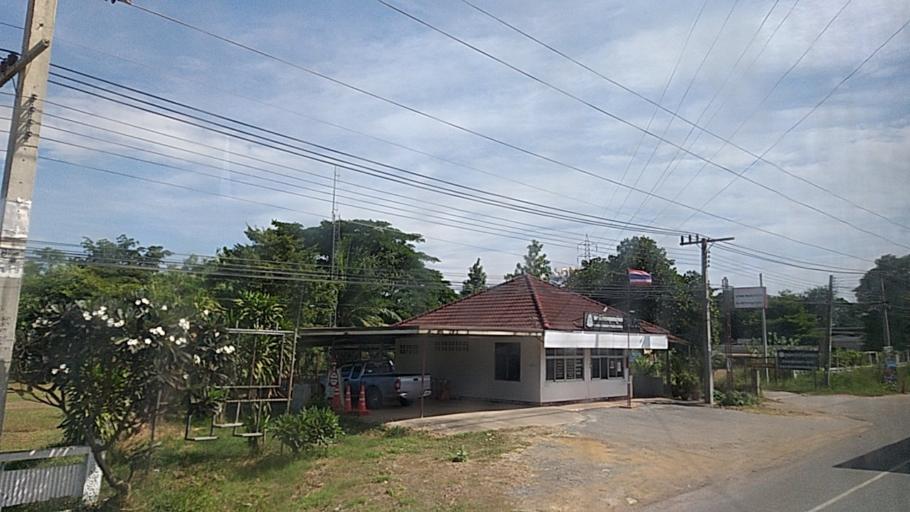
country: TH
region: Khon Kaen
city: Khon Kaen
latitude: 16.4448
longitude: 102.9636
